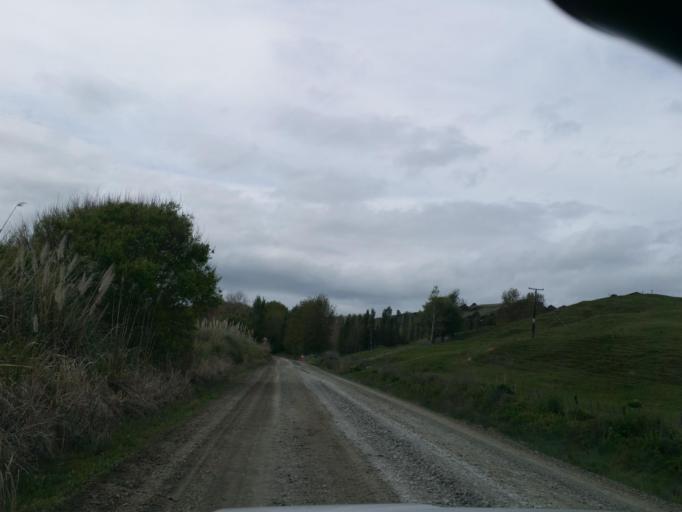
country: NZ
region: Northland
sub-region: Kaipara District
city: Dargaville
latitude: -35.9255
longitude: 173.9215
